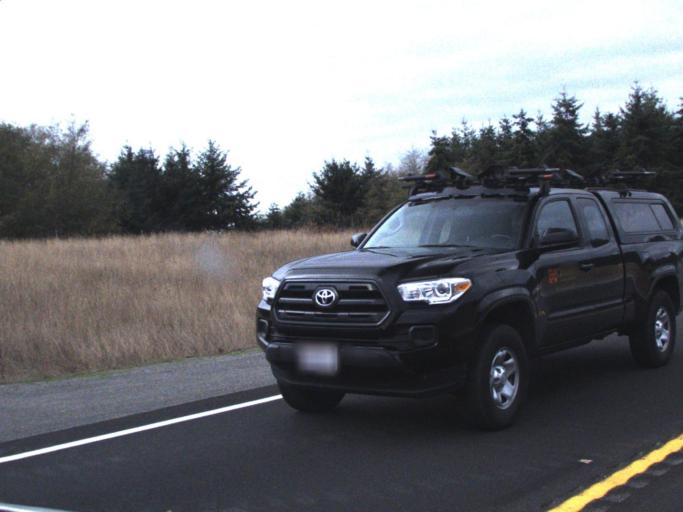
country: US
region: Washington
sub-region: Island County
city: Camano
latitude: 48.1114
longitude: -122.5831
